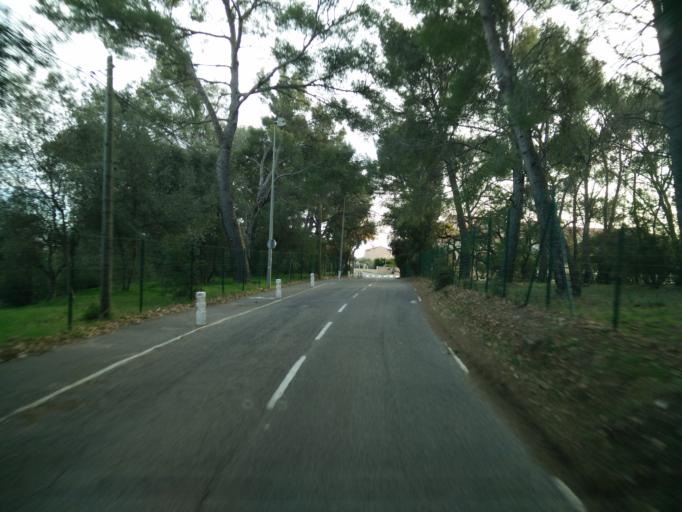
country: FR
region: Provence-Alpes-Cote d'Azur
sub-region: Departement du Var
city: La Londe-les-Maures
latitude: 43.1340
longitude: 6.2297
